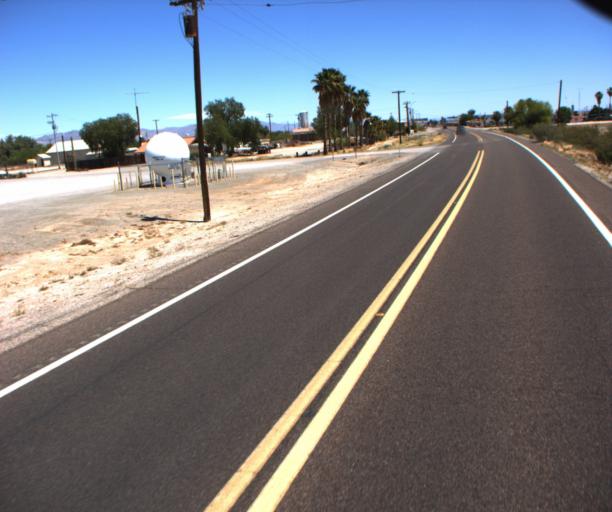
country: US
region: Arizona
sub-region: La Paz County
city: Salome
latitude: 33.7785
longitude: -113.6190
